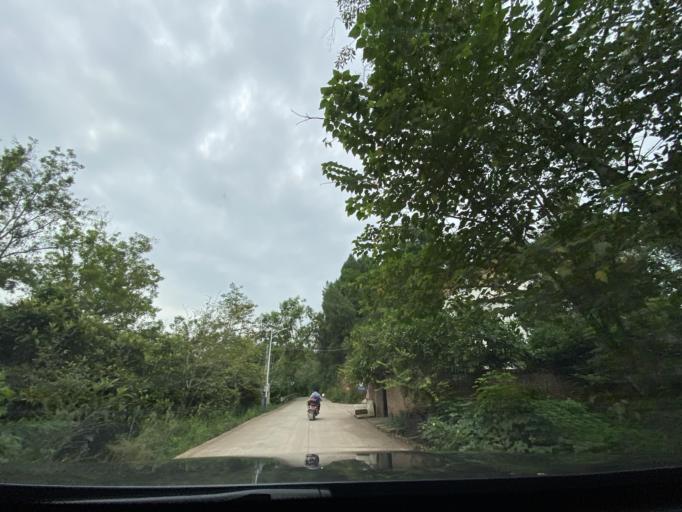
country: CN
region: Sichuan
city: Jiancheng
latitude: 30.3883
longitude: 104.5137
